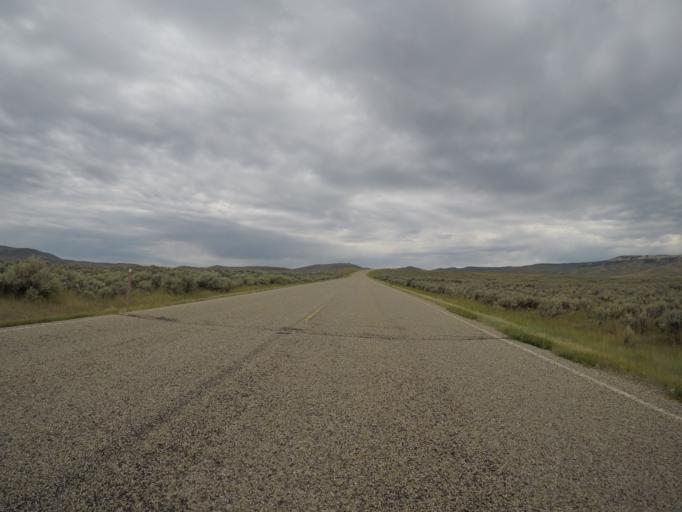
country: US
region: Wyoming
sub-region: Lincoln County
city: Kemmerer
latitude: 41.8258
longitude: -110.7653
